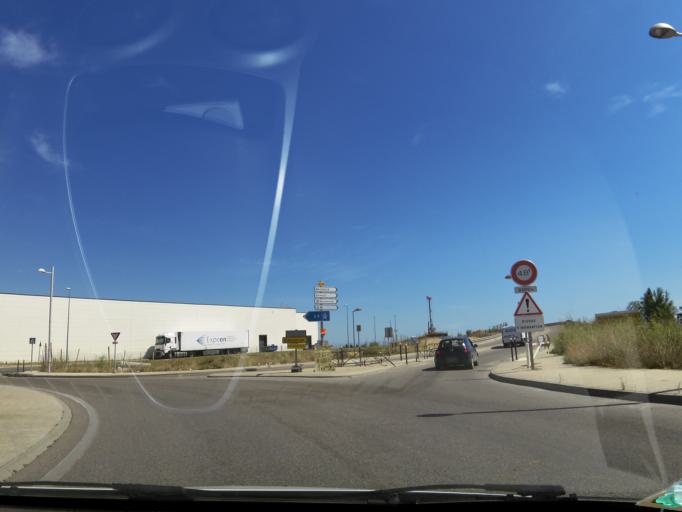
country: FR
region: Languedoc-Roussillon
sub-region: Departement de l'Herault
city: Vendargues
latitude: 43.6507
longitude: 3.9821
